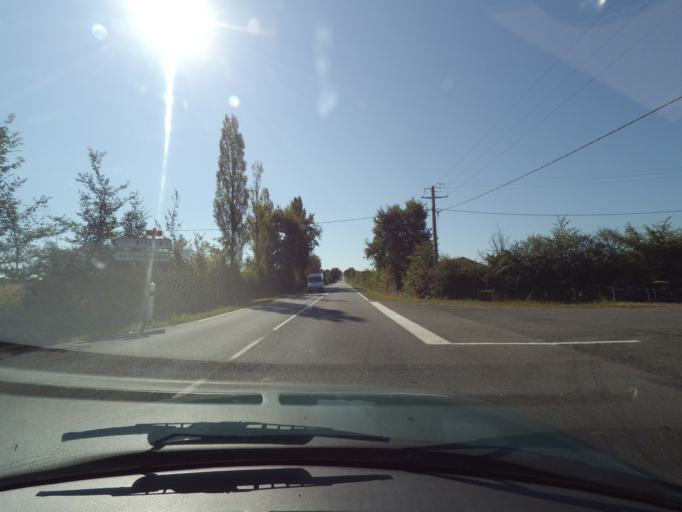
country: FR
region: Poitou-Charentes
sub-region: Departement de la Vienne
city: Lussac-les-Chateaux
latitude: 46.3653
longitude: 0.7700
